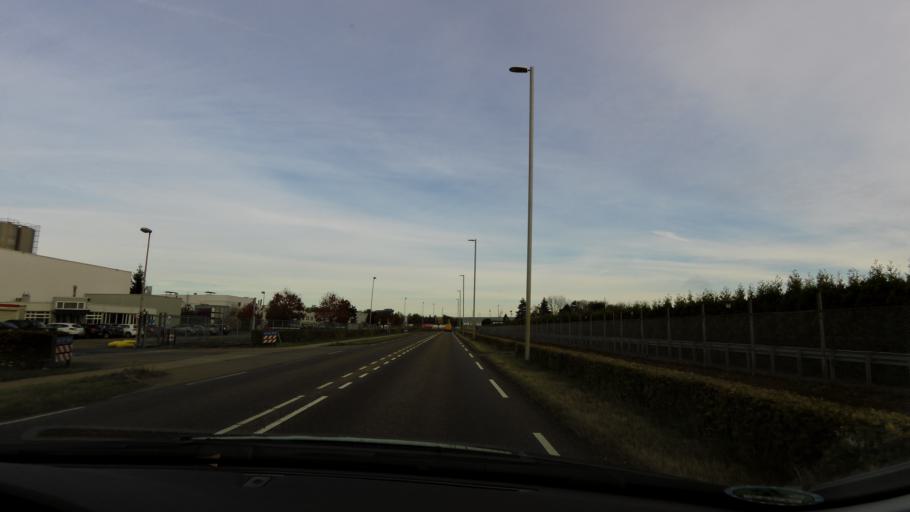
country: NL
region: Limburg
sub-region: Gemeente Sittard-Geleen
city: Born
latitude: 51.0525
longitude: 5.8158
